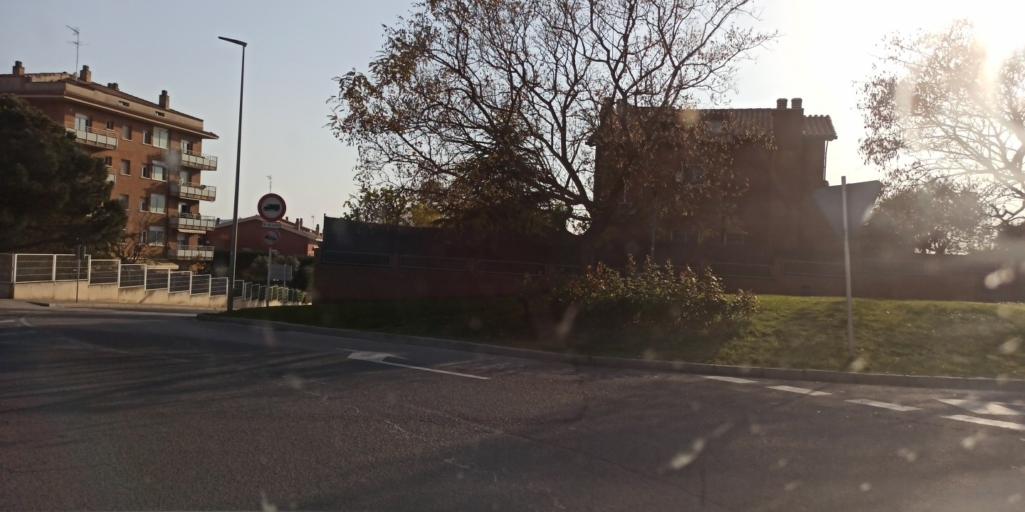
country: ES
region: Catalonia
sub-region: Provincia de Barcelona
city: Sant Feliu de Llobregat
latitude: 41.3929
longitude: 2.0494
